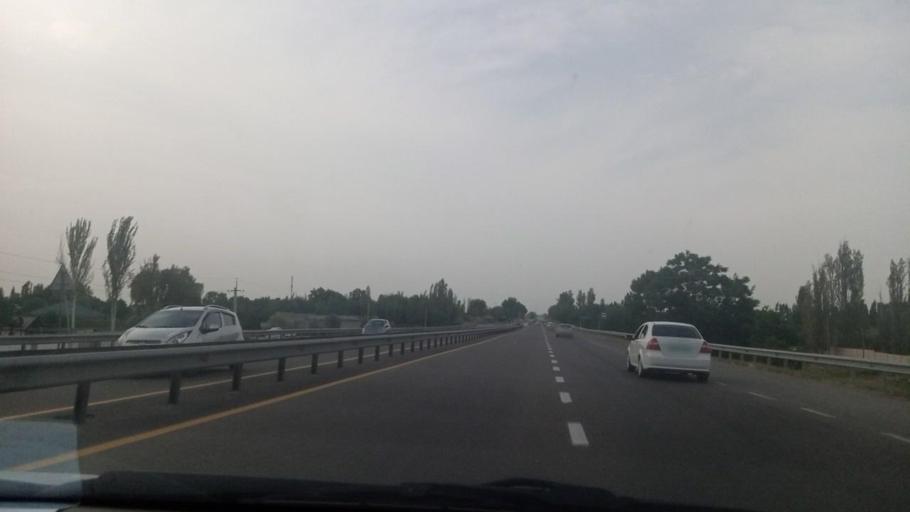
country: UZ
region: Toshkent Shahri
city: Bektemir
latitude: 41.1495
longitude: 69.4282
